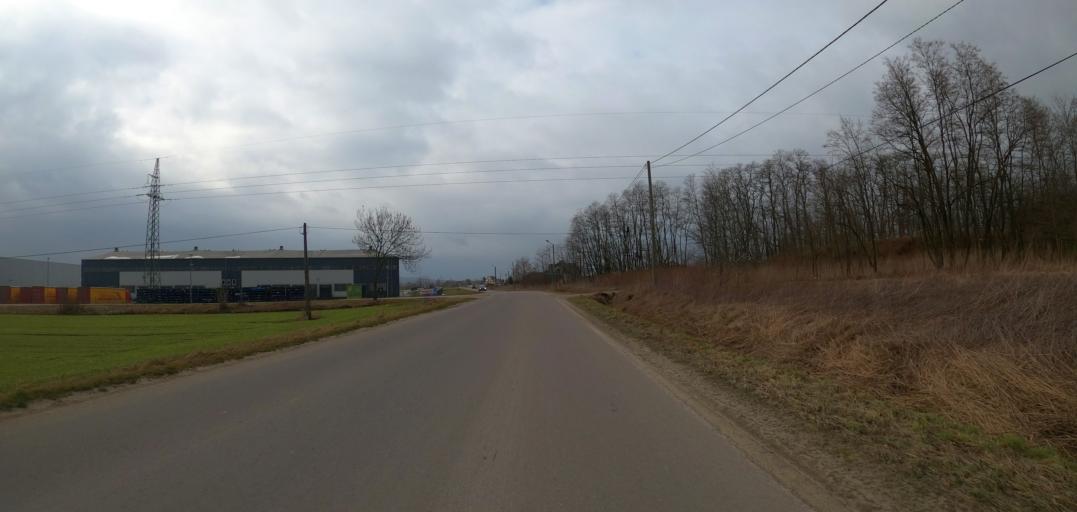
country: PL
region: Subcarpathian Voivodeship
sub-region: Powiat debicki
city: Pilzno
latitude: 49.9869
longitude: 21.3224
